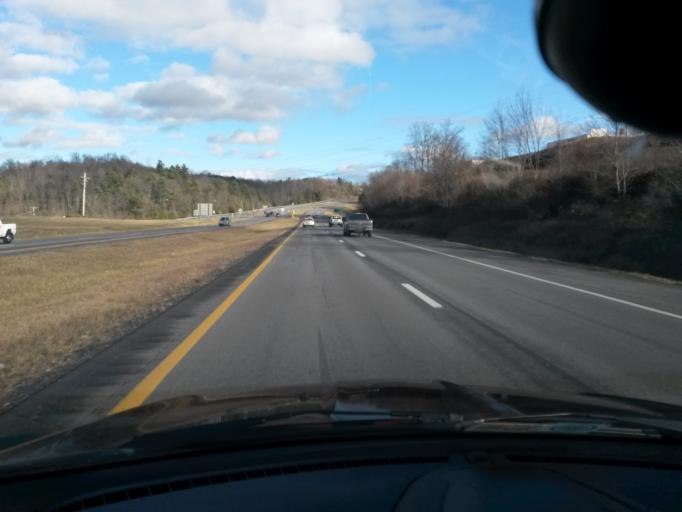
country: US
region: West Virginia
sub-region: Mercer County
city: Princeton
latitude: 37.3640
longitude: -81.0405
